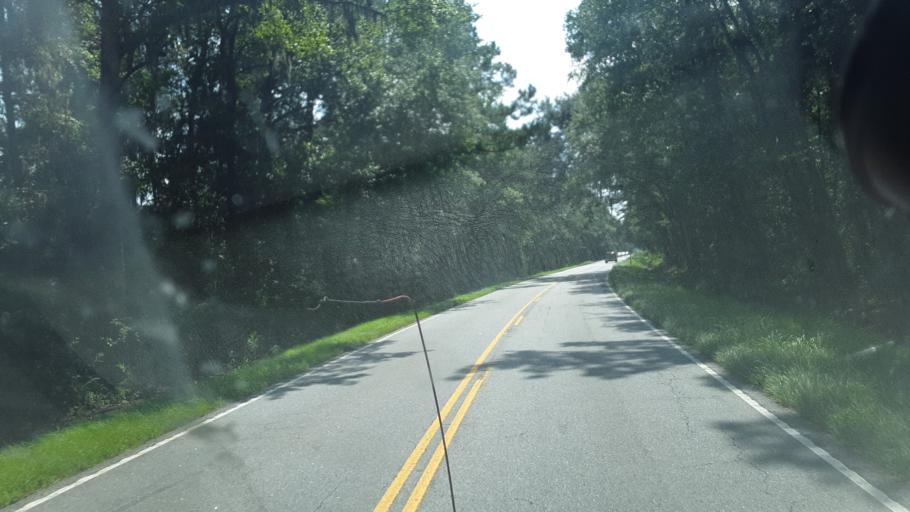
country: US
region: Georgia
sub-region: Chatham County
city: Savannah
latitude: 32.1748
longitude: -81.0292
